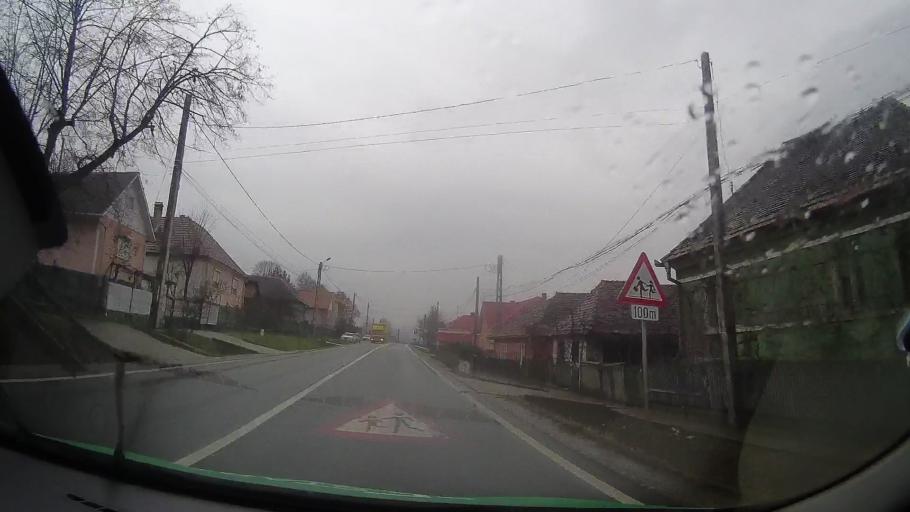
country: RO
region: Bistrita-Nasaud
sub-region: Comuna Galatii Bistritei
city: Galatii Bistritei
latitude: 46.9931
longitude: 24.4207
